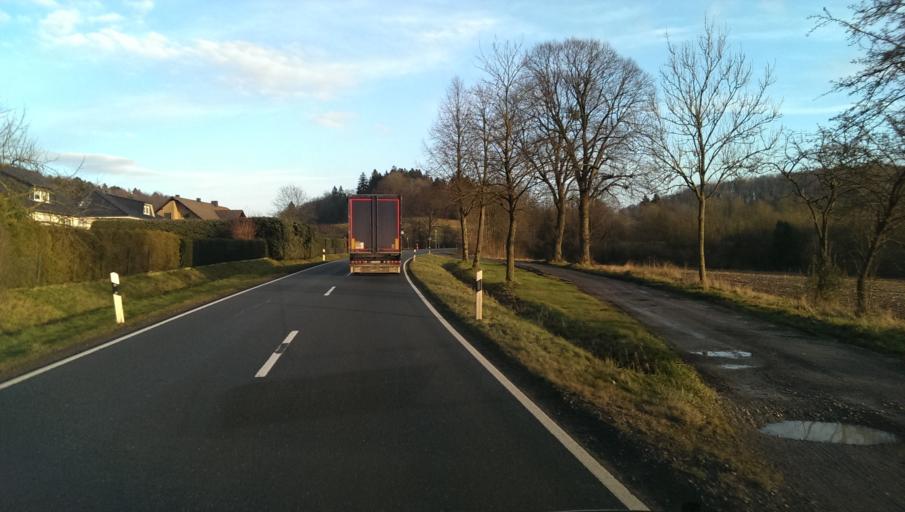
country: DE
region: Lower Saxony
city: Stadtoldendorf
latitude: 51.8798
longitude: 9.6443
